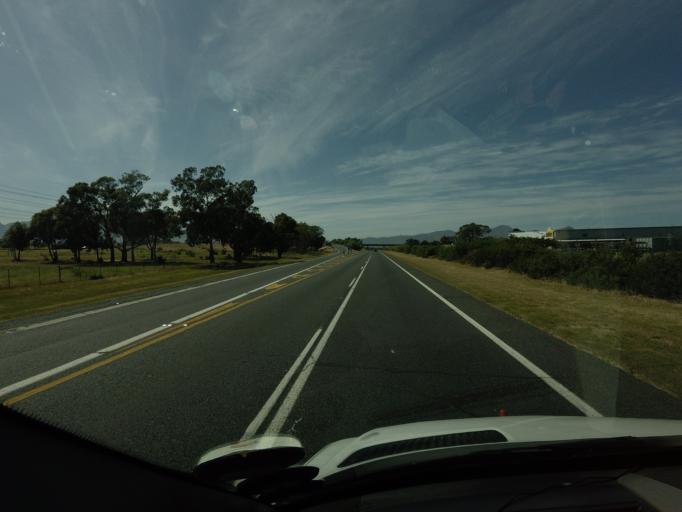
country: ZA
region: Western Cape
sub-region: Cape Winelands District Municipality
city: Stellenbosch
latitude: -34.0751
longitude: 18.8190
